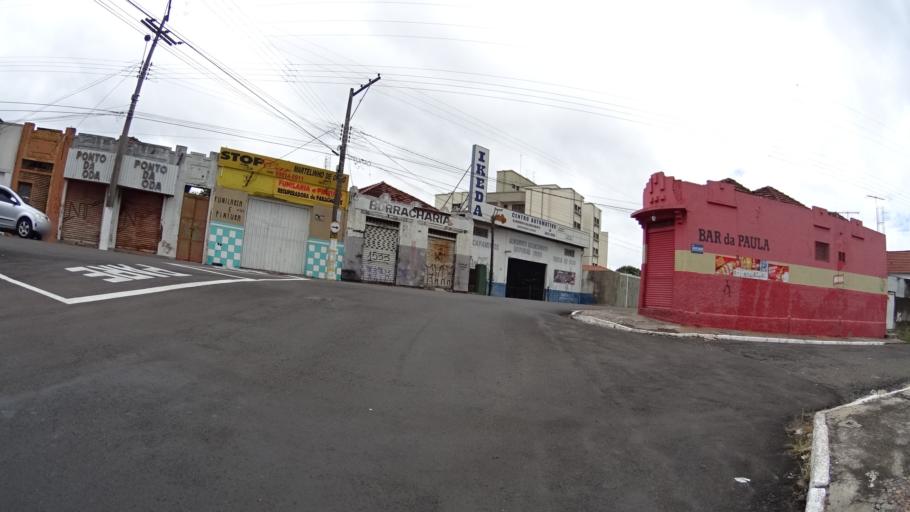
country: BR
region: Sao Paulo
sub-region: Marilia
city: Marilia
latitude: -22.2222
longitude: -49.9568
